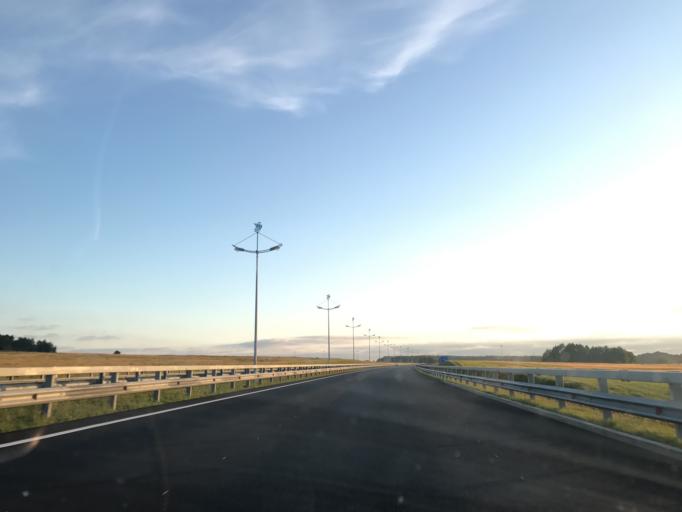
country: RU
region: Kaliningrad
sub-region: Gorod Kaliningrad
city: Pionerskiy
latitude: 54.9099
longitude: 20.2167
